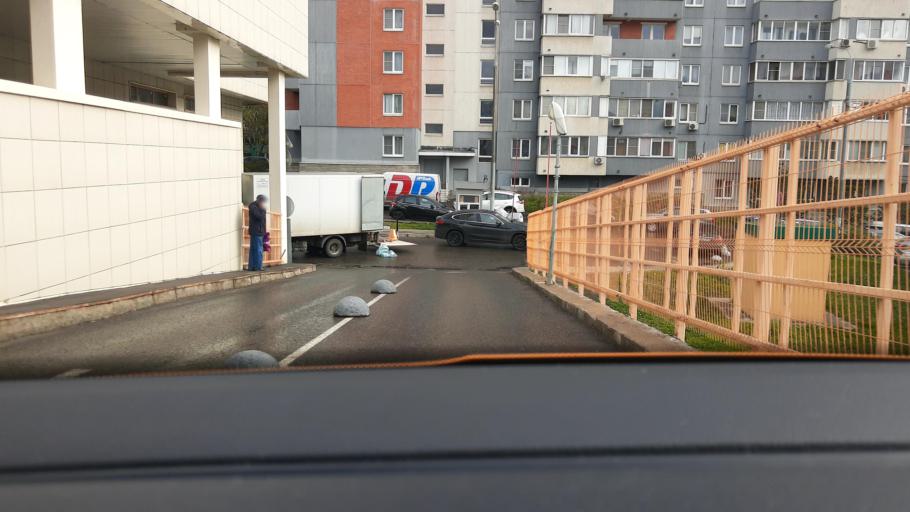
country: RU
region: Moscow
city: Strogino
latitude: 55.7982
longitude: 37.3900
